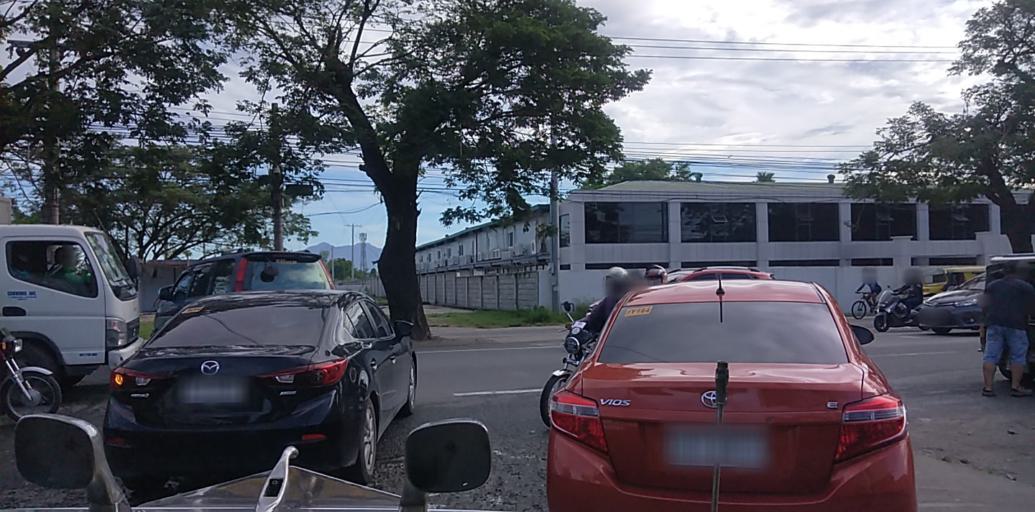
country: PH
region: Central Luzon
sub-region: Province of Pampanga
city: Telabastagan
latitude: 15.1095
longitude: 120.6128
